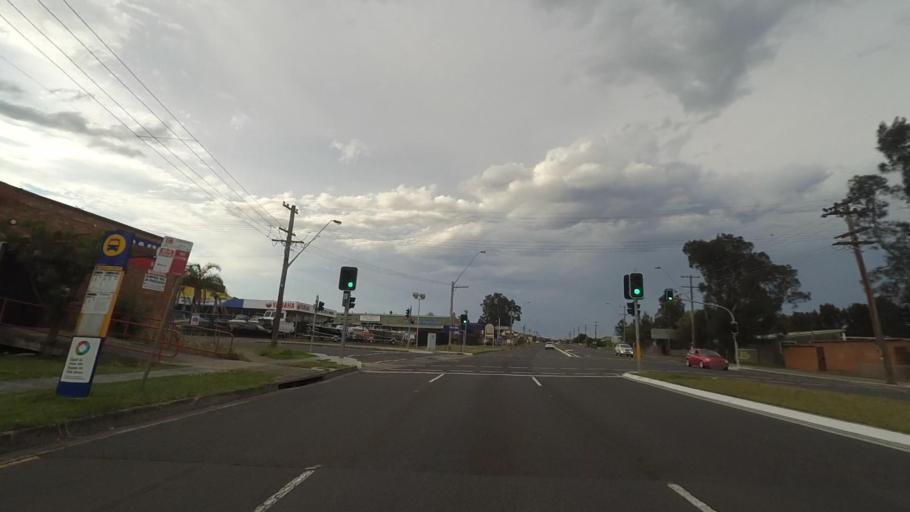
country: AU
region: New South Wales
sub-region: Shellharbour
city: Barrack Heights
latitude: -34.5582
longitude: 150.8595
